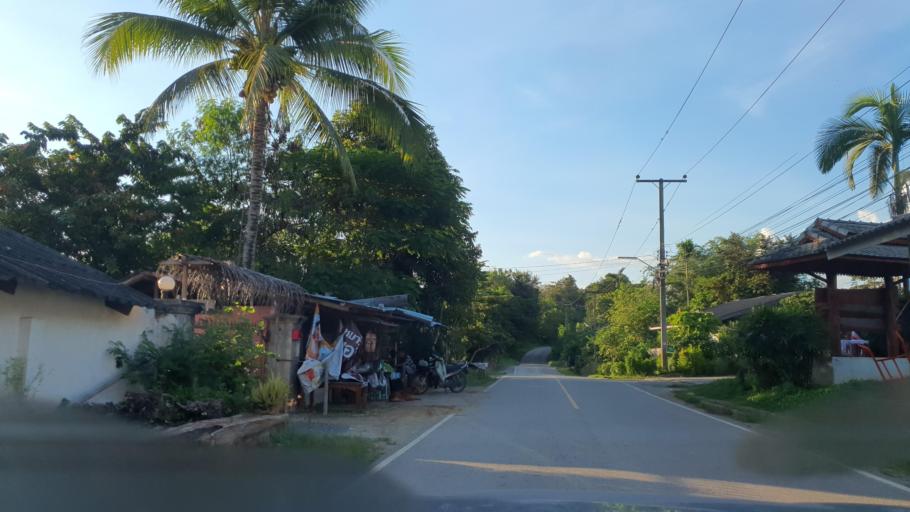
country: TH
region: Chiang Mai
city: Mae On
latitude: 18.8404
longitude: 99.2807
